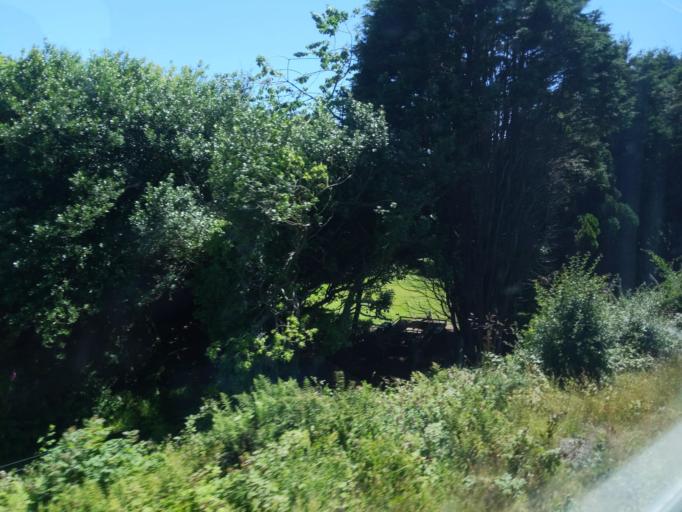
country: GB
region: England
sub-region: Cornwall
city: Chacewater
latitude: 50.2635
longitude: -5.1859
